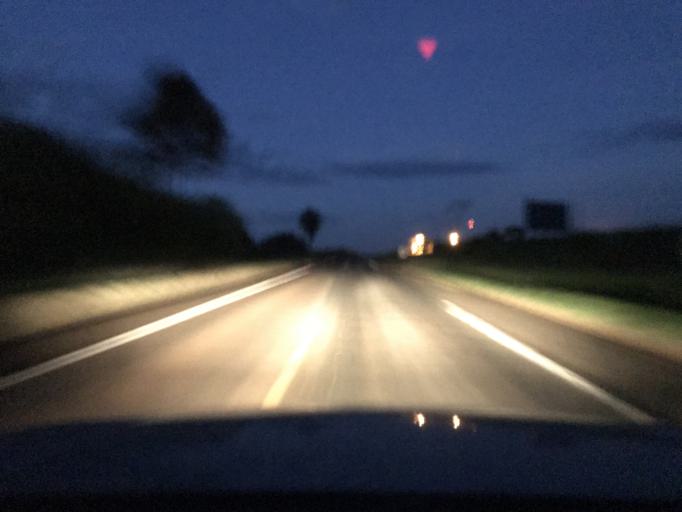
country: PY
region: Canindeyu
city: Salto del Guaira
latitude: -24.1034
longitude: -54.2325
